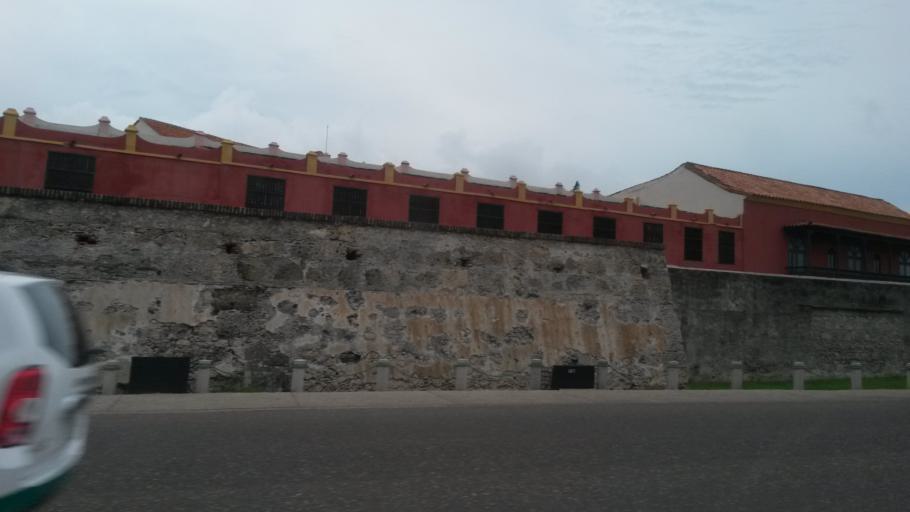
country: CO
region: Bolivar
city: Cartagena
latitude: 10.4264
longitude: -75.5525
